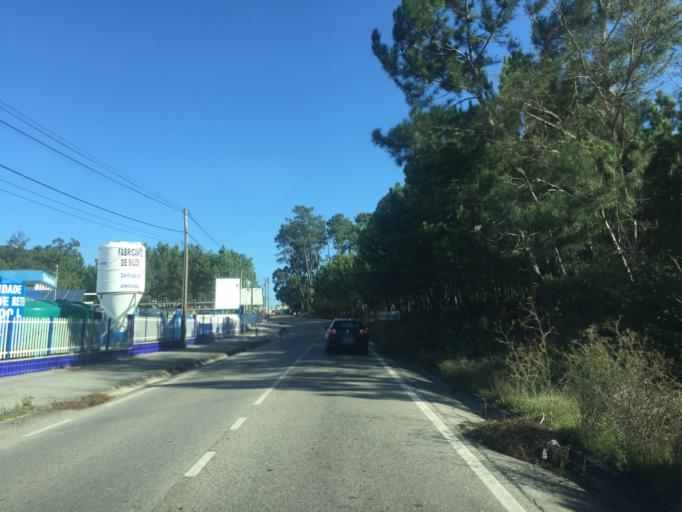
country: PT
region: Leiria
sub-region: Leiria
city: Amor
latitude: 39.8175
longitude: -8.8422
